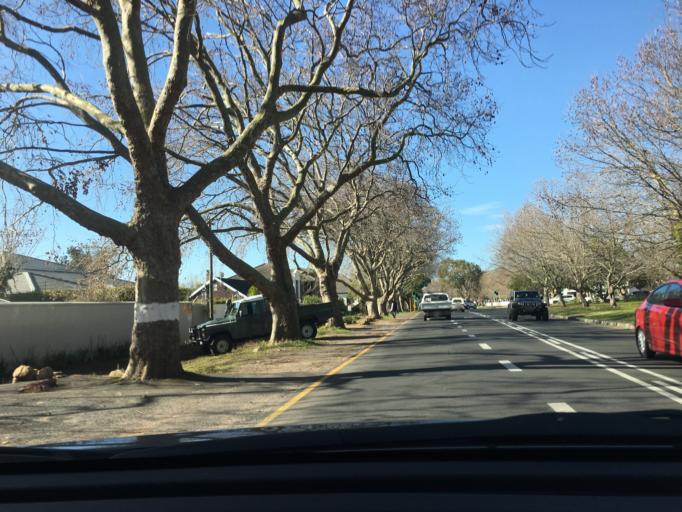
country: ZA
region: Western Cape
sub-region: City of Cape Town
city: Constantia
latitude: -34.0205
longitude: 18.4431
